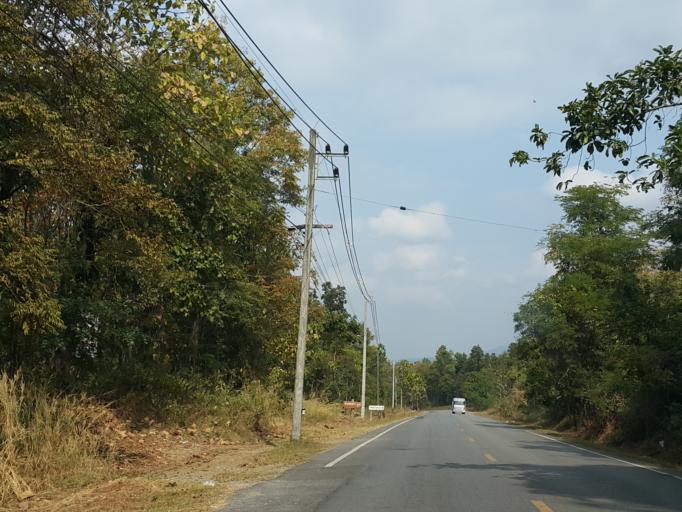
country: TH
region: Chiang Mai
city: Mae On
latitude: 18.8359
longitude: 99.2624
